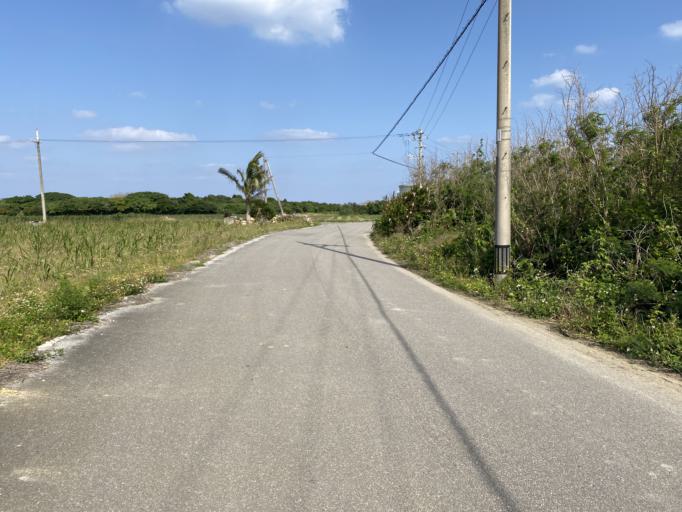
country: JP
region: Okinawa
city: Ishigaki
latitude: 24.0581
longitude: 123.7847
